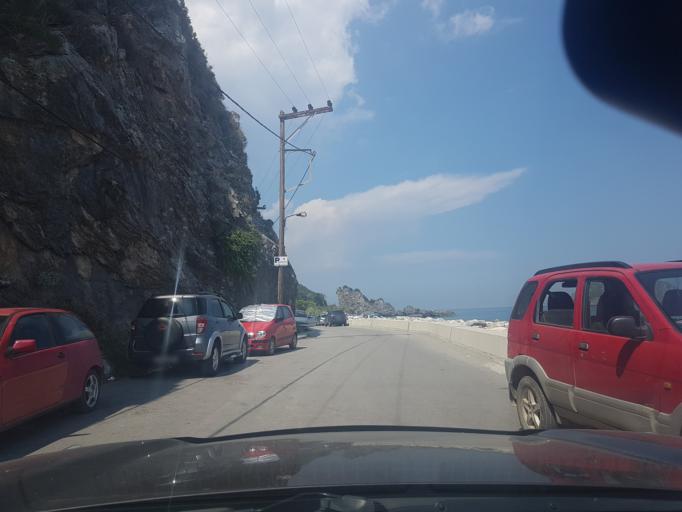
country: GR
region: Central Greece
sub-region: Nomos Evvoias
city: Kymi
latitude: 38.6693
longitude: 23.9240
